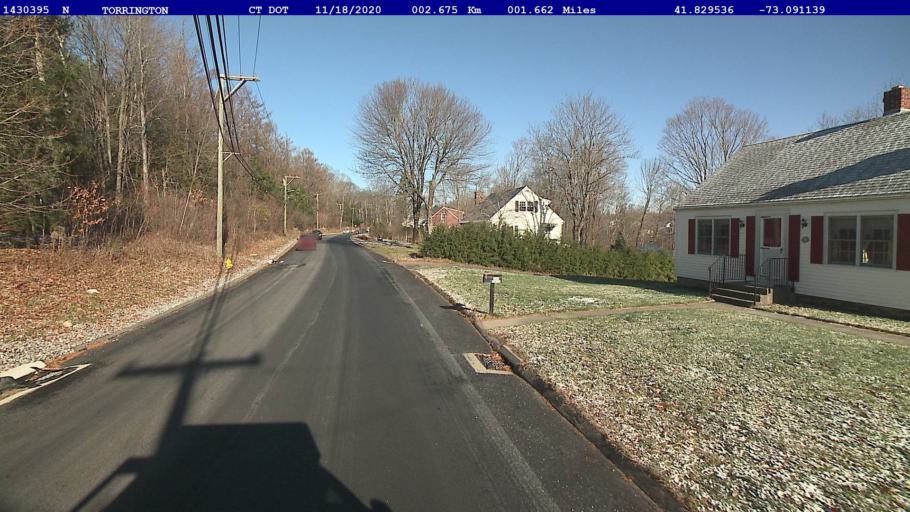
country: US
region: Connecticut
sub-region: Litchfield County
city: Torrington
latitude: 41.8295
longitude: -73.0912
